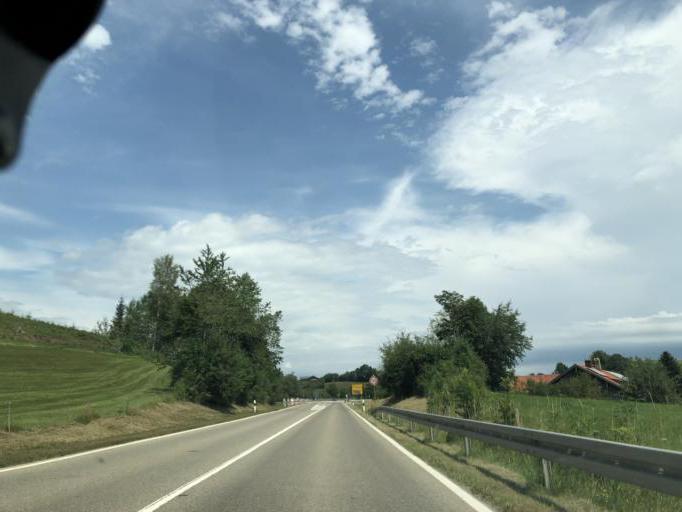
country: DE
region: Bavaria
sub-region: Swabia
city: Oy-Mittelberg
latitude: 47.6313
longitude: 10.4565
